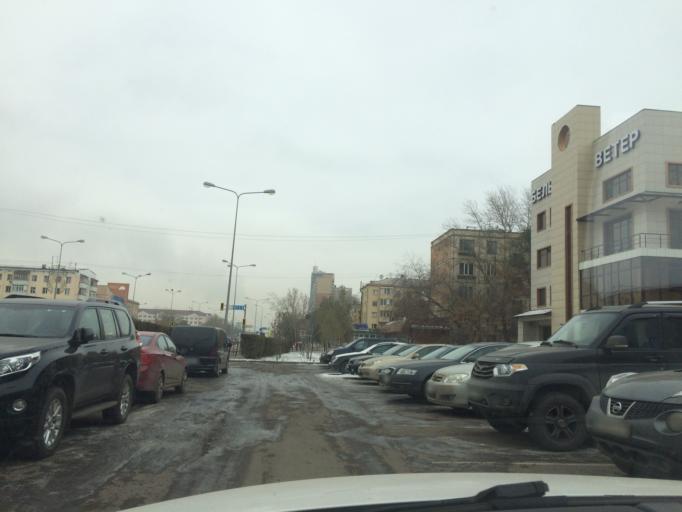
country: KZ
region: Astana Qalasy
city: Astana
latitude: 51.1762
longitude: 71.4168
